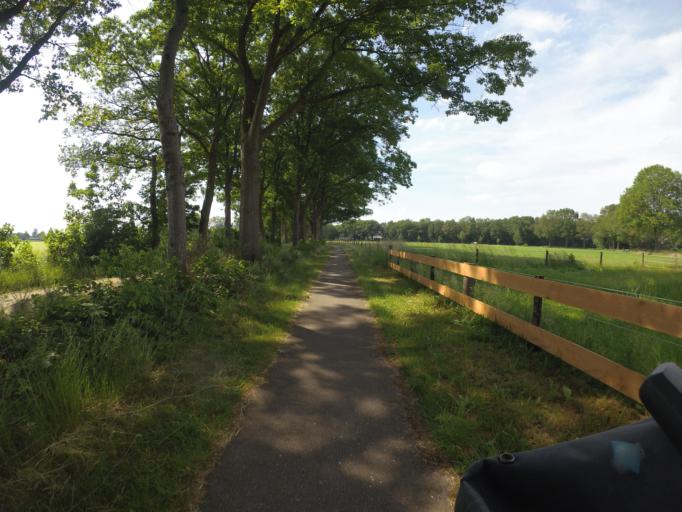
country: NL
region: Overijssel
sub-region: Gemeente Raalte
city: Raalte
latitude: 52.4371
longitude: 6.3078
